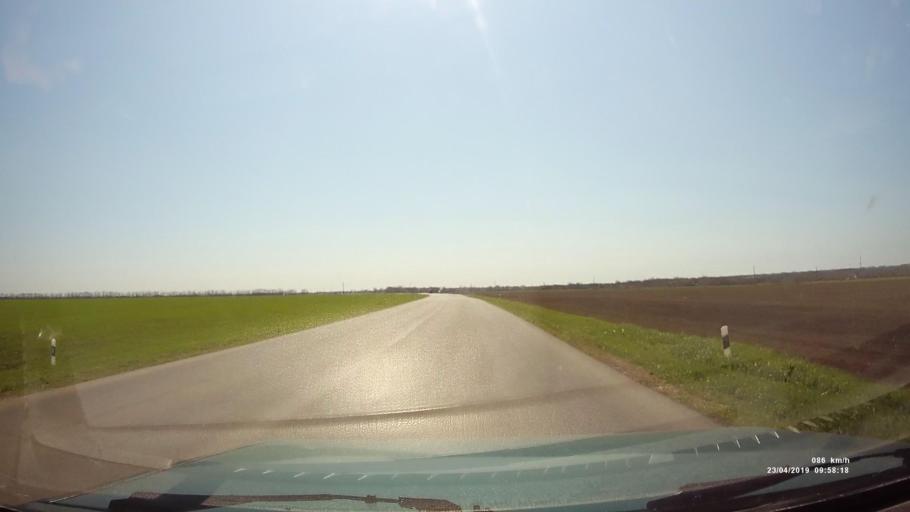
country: RU
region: Rostov
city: Sovetskoye
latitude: 46.7809
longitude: 42.0973
